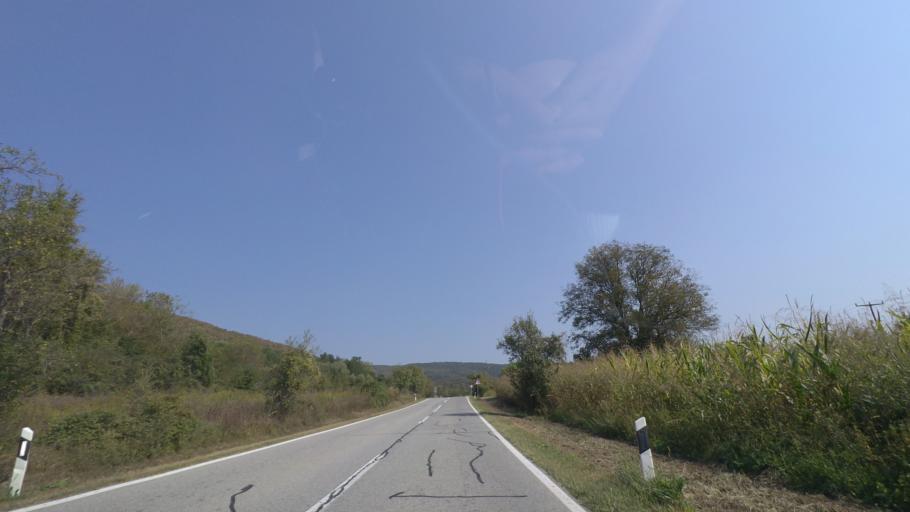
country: HR
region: Pozesko-Slavonska
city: Velika
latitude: 45.4185
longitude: 17.5025
